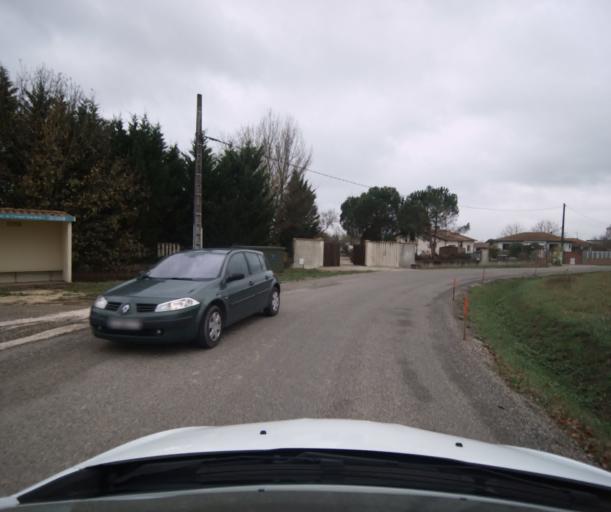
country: FR
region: Midi-Pyrenees
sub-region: Departement du Tarn-et-Garonne
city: Castelsarrasin
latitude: 44.0637
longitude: 1.1383
